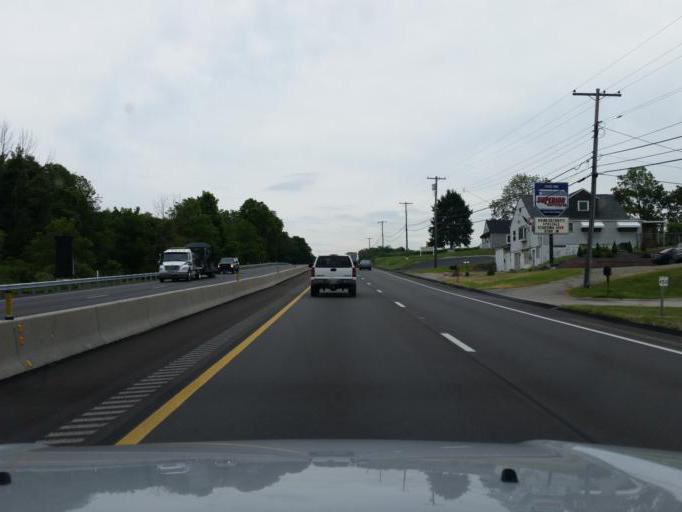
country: US
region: Pennsylvania
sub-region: Westmoreland County
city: Lawson Heights
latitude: 40.2840
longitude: -79.4258
